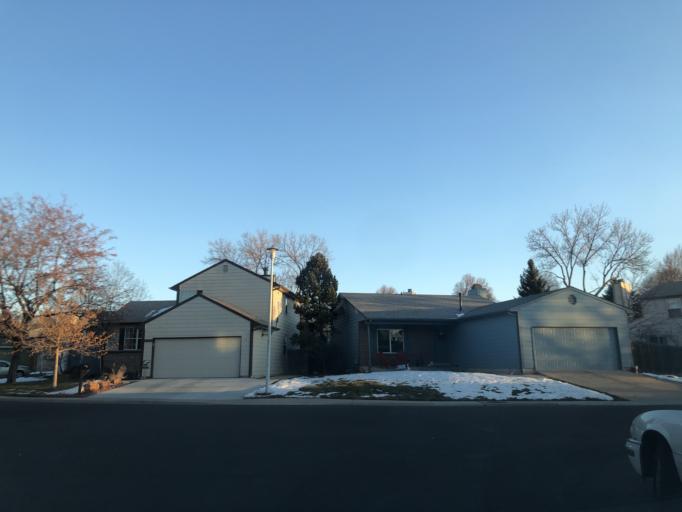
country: US
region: Colorado
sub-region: Adams County
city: Aurora
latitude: 39.7060
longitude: -104.8048
